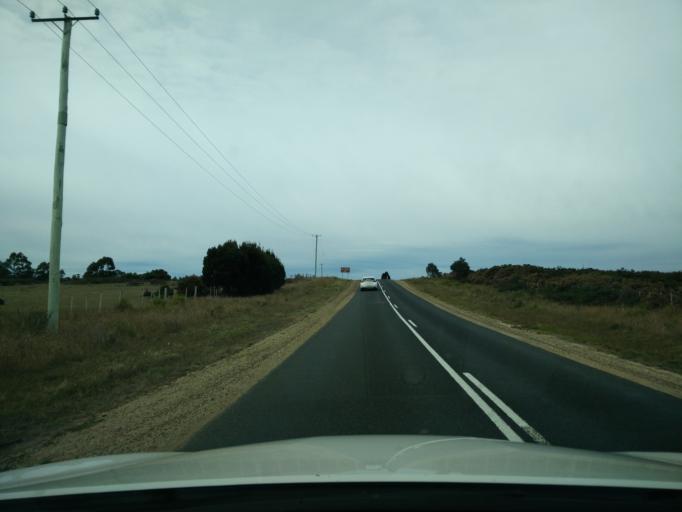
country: AU
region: Tasmania
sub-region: Break O'Day
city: St Helens
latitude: -41.9378
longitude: 148.2218
